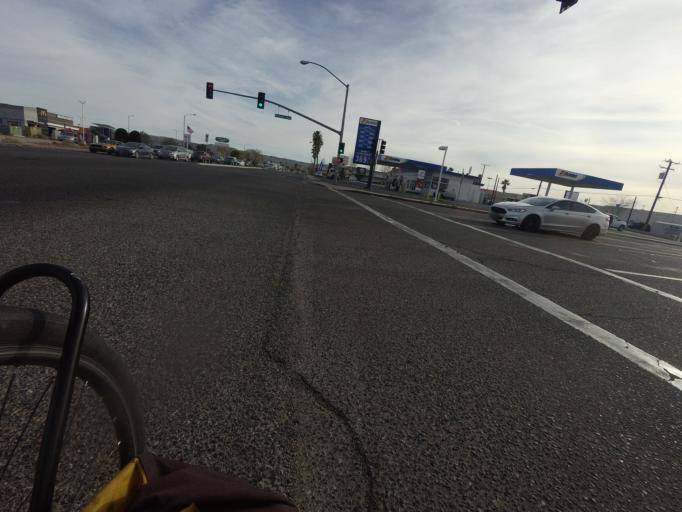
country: US
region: California
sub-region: Kern County
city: Ridgecrest
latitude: 35.6248
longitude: -117.6701
